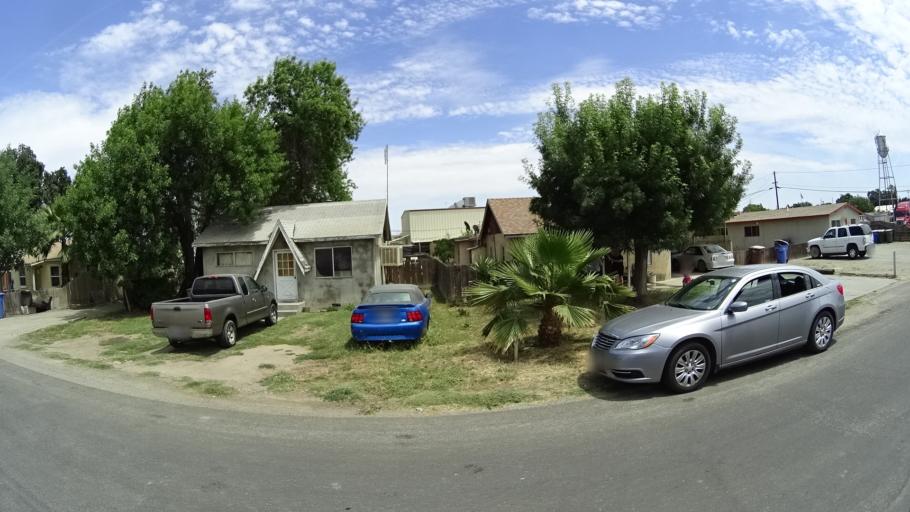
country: US
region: California
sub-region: Kings County
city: Armona
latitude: 36.3160
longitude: -119.7104
